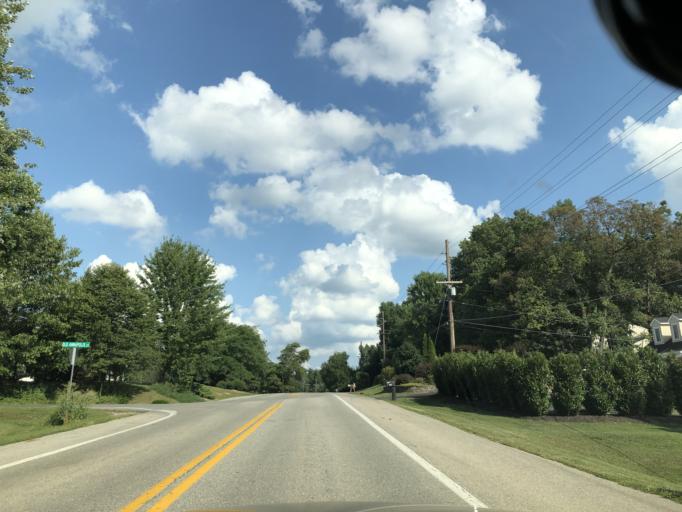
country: US
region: Maryland
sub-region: Carroll County
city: Mount Airy
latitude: 39.3980
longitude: -77.1901
